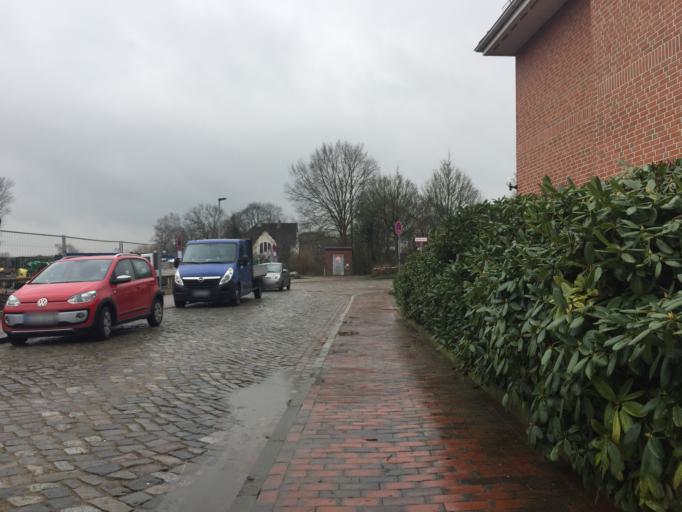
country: DE
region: Schleswig-Holstein
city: Itzehoe
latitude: 53.9181
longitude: 9.5158
